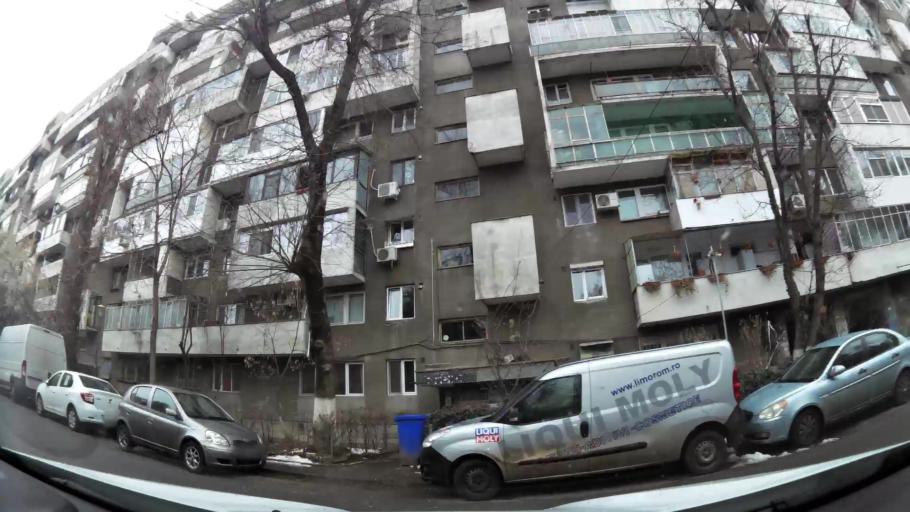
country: RO
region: Ilfov
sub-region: Comuna Chiajna
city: Rosu
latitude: 44.4245
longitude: 26.0273
